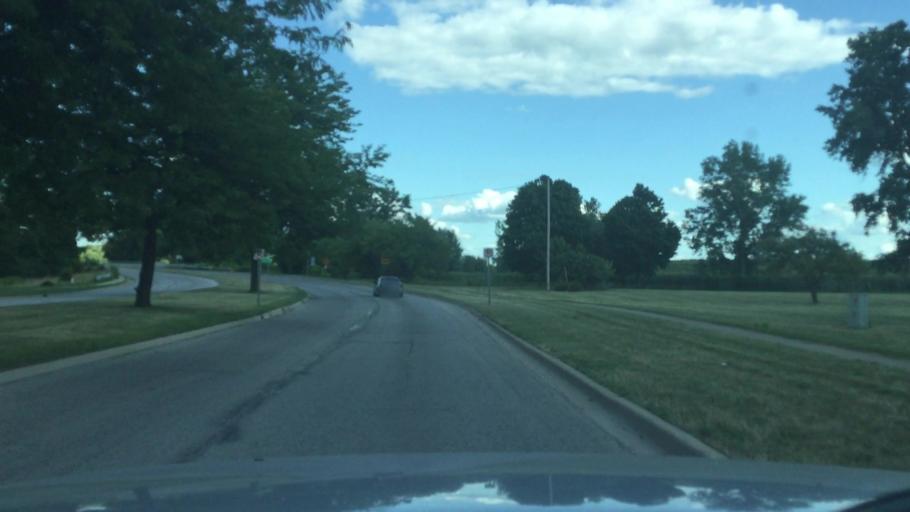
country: US
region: Michigan
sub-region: Saginaw County
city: Saginaw
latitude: 43.4030
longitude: -83.9693
